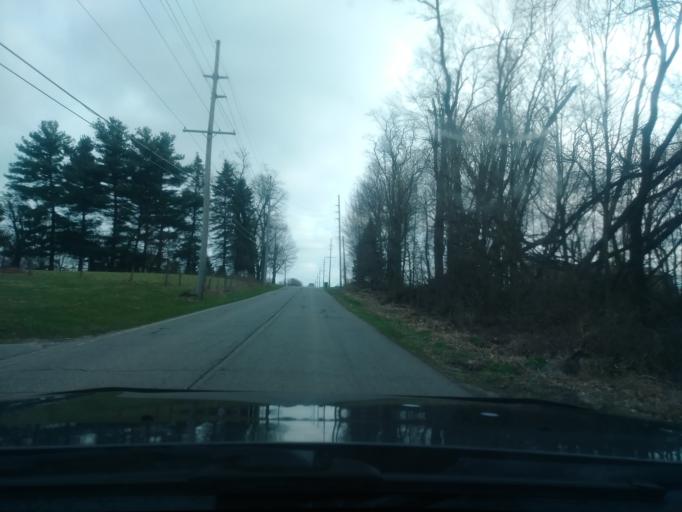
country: US
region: Indiana
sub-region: LaPorte County
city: LaPorte
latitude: 41.6224
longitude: -86.7965
